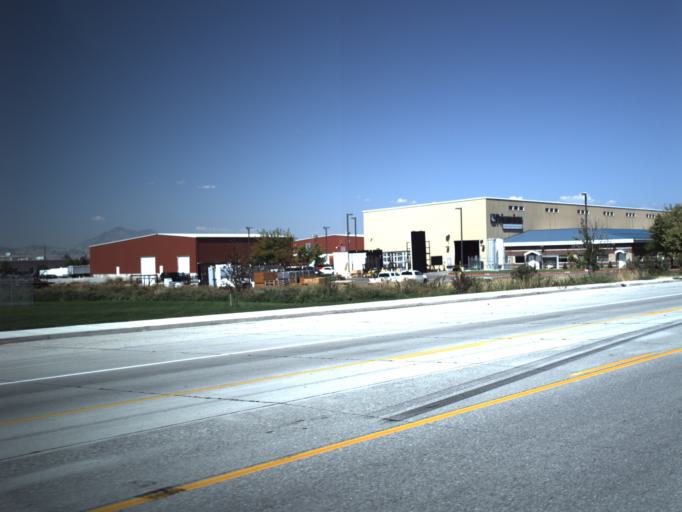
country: US
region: Utah
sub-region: Cache County
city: Logan
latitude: 41.7610
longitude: -111.8586
